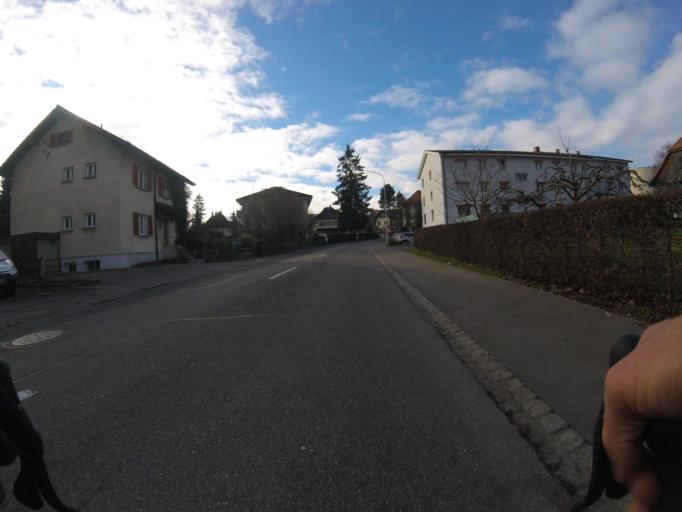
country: CH
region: Bern
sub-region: Bern-Mittelland District
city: Bolligen
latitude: 46.9550
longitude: 7.4892
